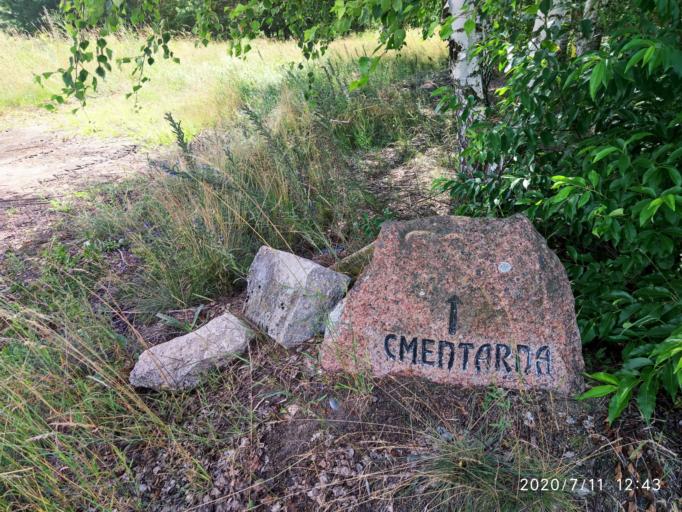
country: PL
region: Lubusz
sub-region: Powiat krosnienski
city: Maszewo
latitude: 52.0132
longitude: 14.9568
